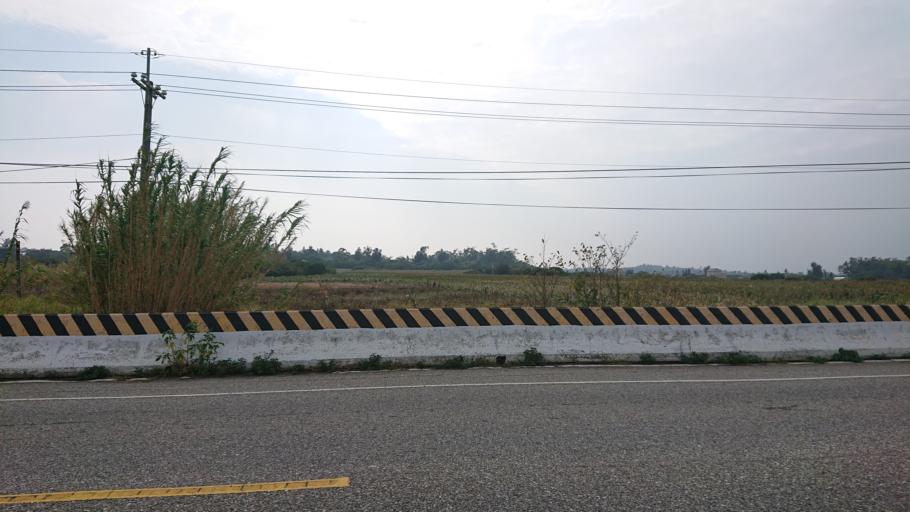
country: TW
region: Fukien
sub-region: Kinmen
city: Jincheng
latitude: 24.4516
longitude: 118.3814
